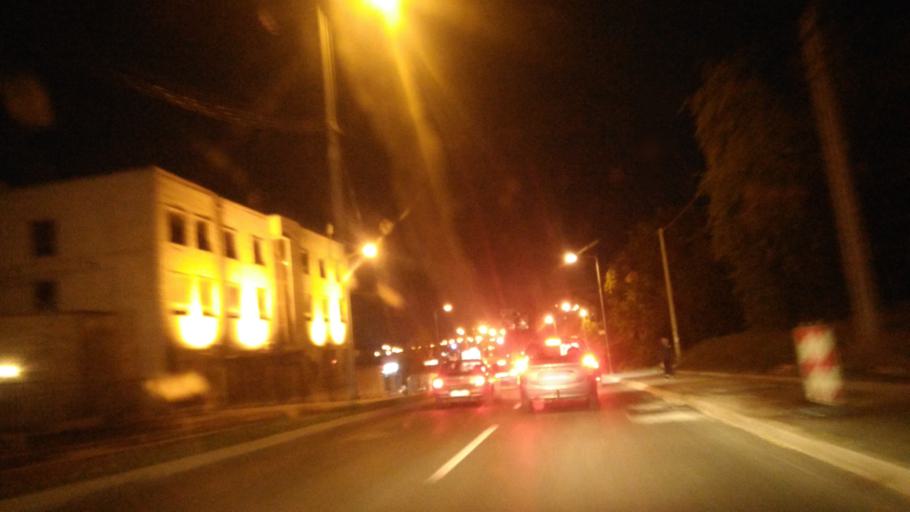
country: RS
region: Central Serbia
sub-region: Belgrade
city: Cukarica
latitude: 44.7718
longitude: 20.4096
